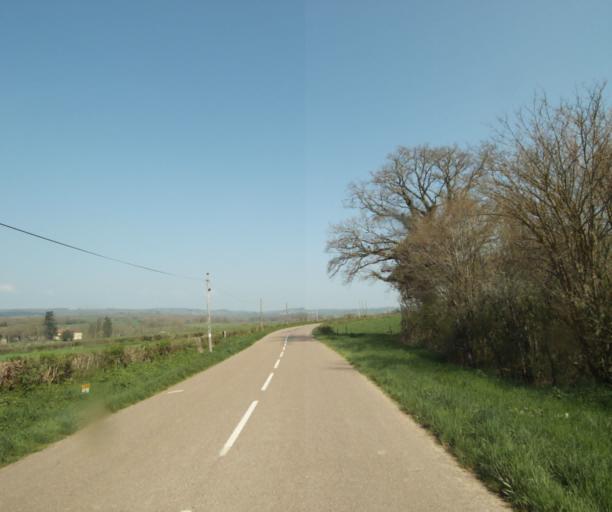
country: FR
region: Bourgogne
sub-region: Departement de Saone-et-Loire
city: Charolles
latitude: 46.4852
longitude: 4.3444
